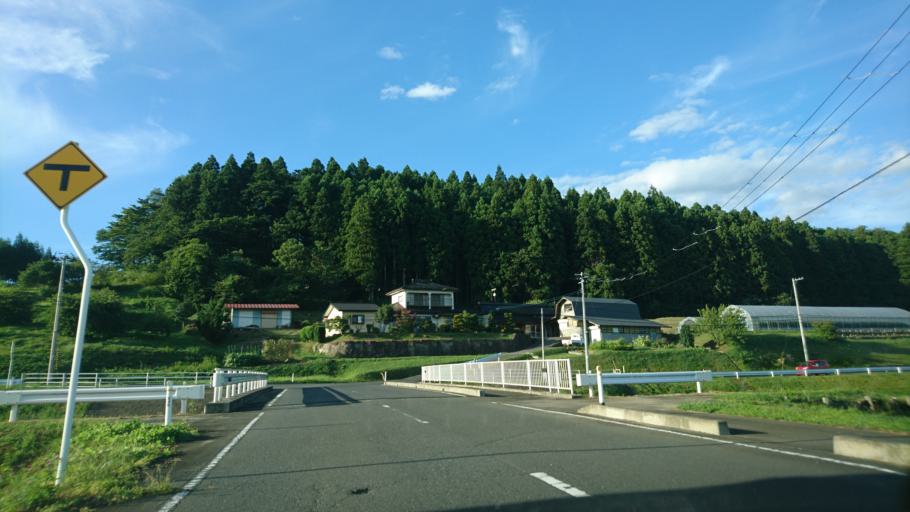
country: JP
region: Iwate
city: Ichinoseki
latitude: 38.8505
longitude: 141.0996
